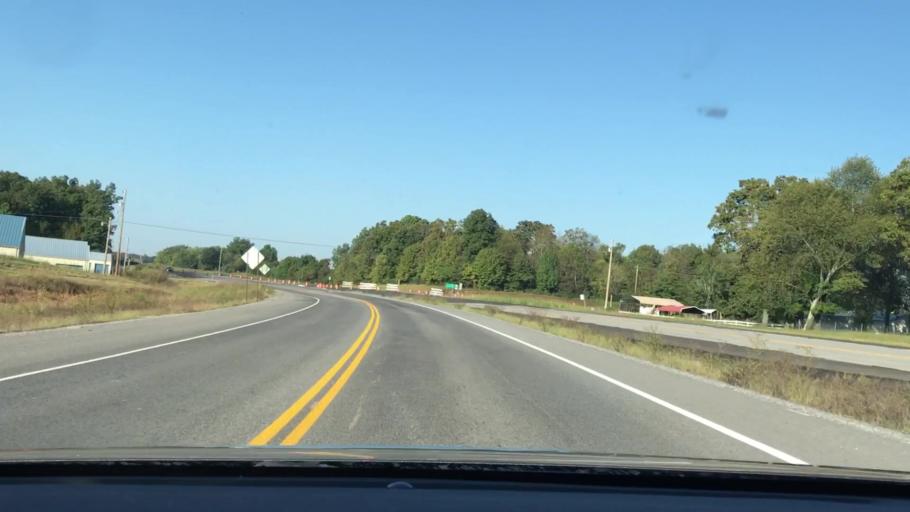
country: US
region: Kentucky
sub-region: Trigg County
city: Cadiz
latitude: 36.8393
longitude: -87.8581
